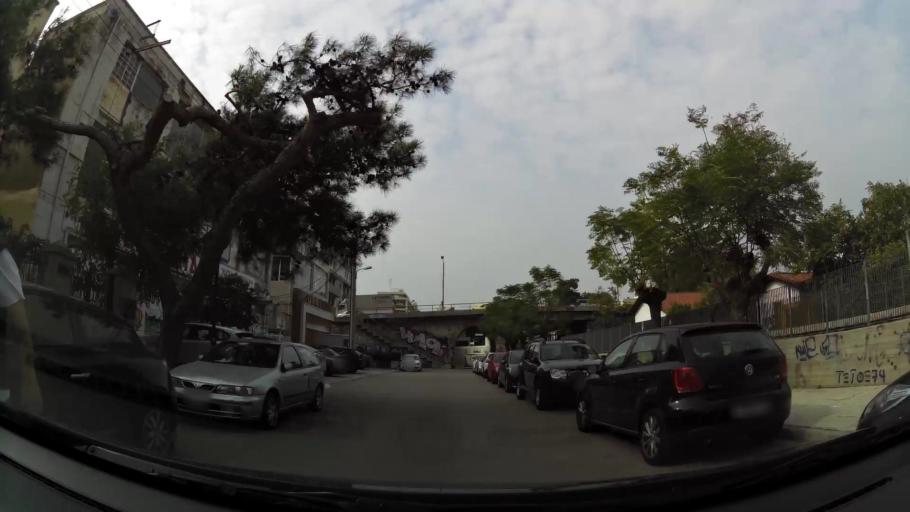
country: GR
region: Attica
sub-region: Nomarchia Athinas
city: Kallithea
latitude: 37.9607
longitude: 23.6982
